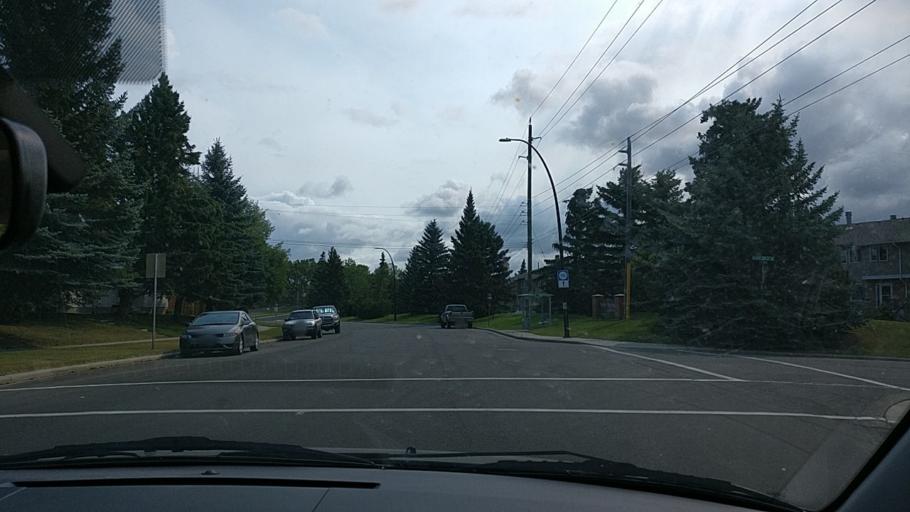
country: CA
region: Alberta
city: Calgary
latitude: 51.1035
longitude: -114.1946
